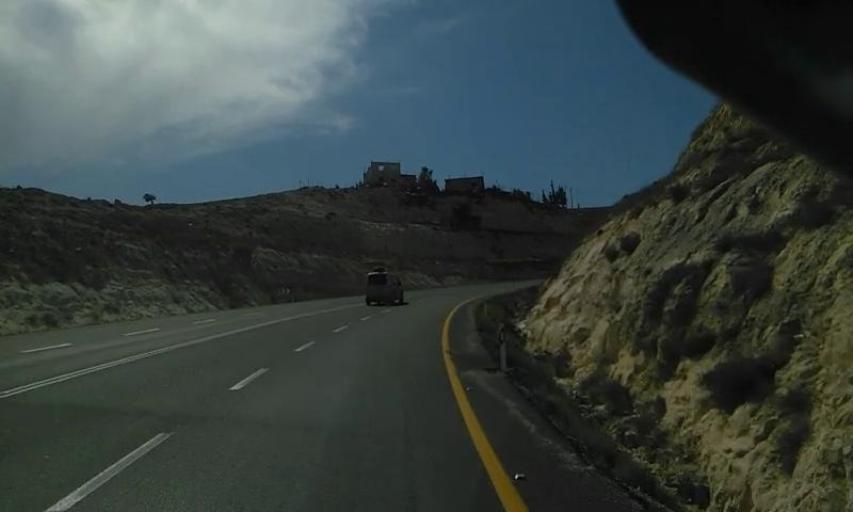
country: PS
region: West Bank
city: Bayt Ta`mar
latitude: 31.6733
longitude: 35.2434
